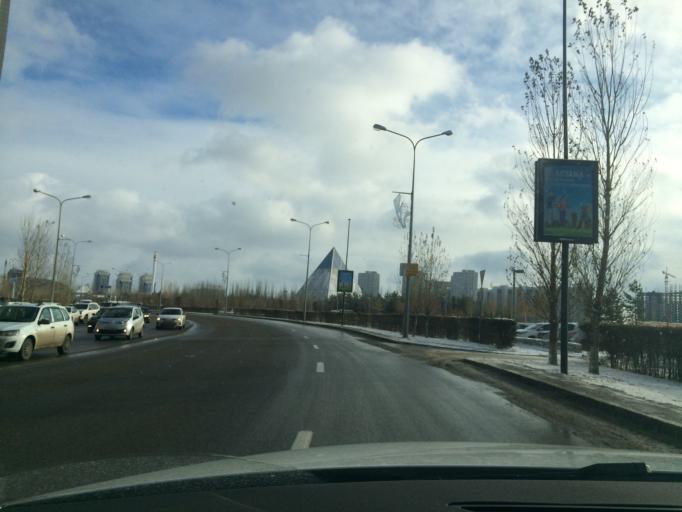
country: KZ
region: Astana Qalasy
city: Astana
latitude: 51.1279
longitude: 71.4583
